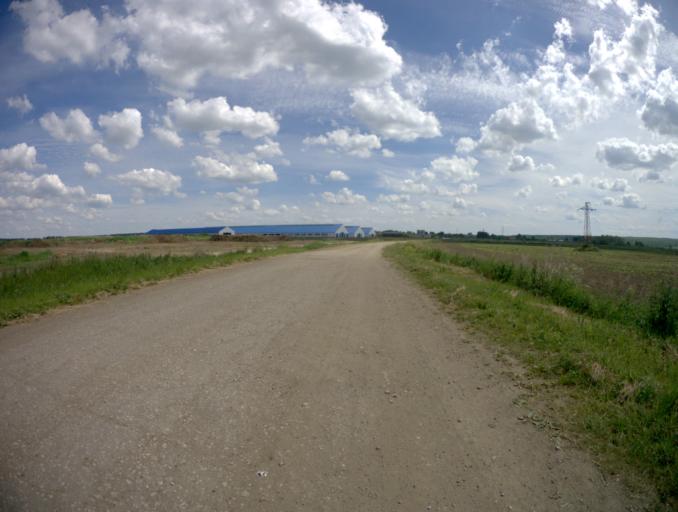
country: RU
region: Vladimir
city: Stavrovo
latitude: 56.3619
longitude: 39.9686
